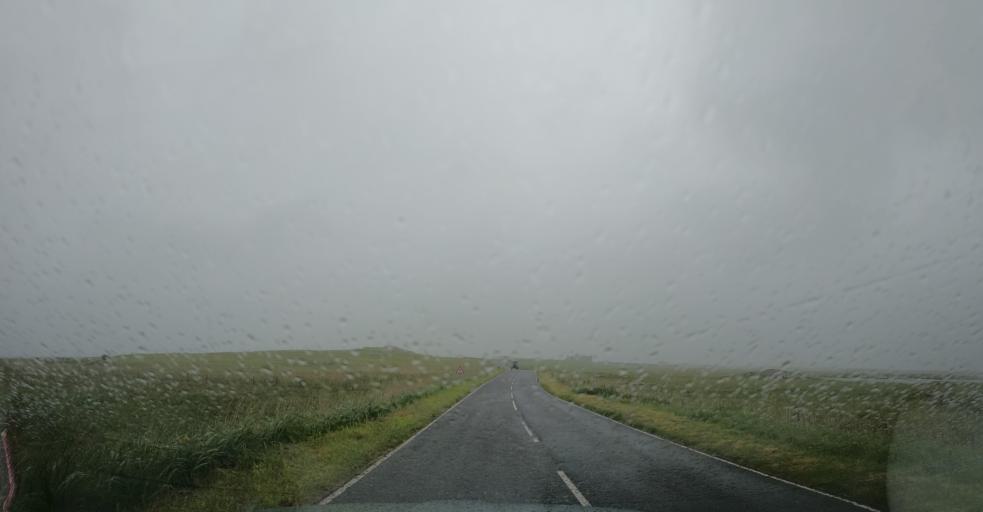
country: GB
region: Scotland
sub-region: Eilean Siar
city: Benbecula
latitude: 57.4537
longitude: -7.4043
